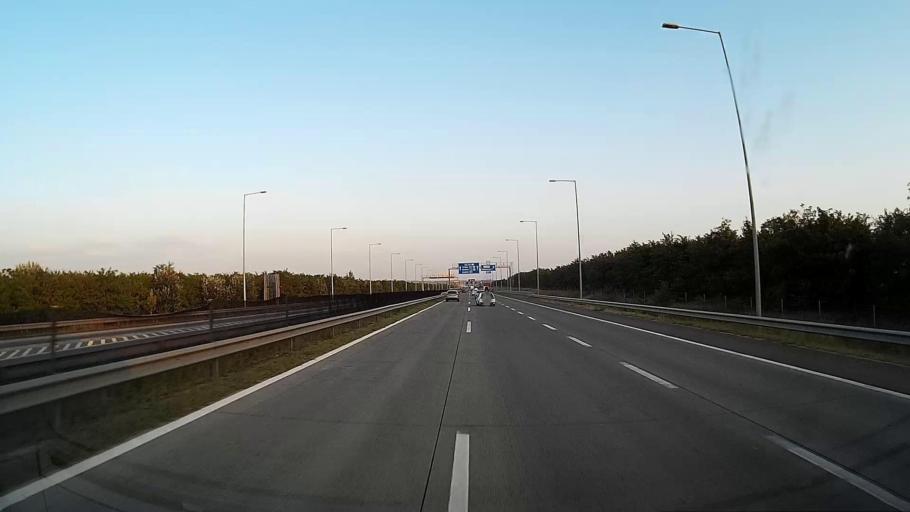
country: HU
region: Pest
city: Kistarcsa
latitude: 47.5299
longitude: 19.2501
